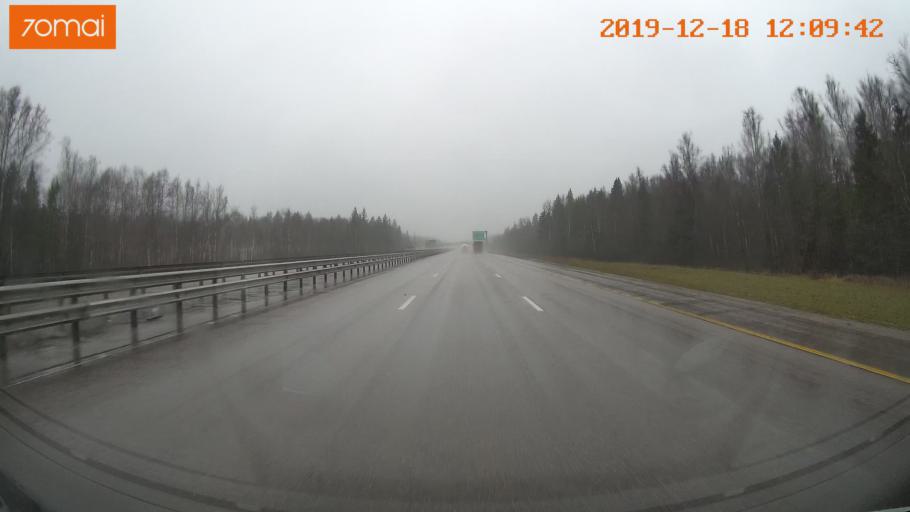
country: RU
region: Moskovskaya
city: Kostrovo
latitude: 55.9117
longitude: 36.6088
